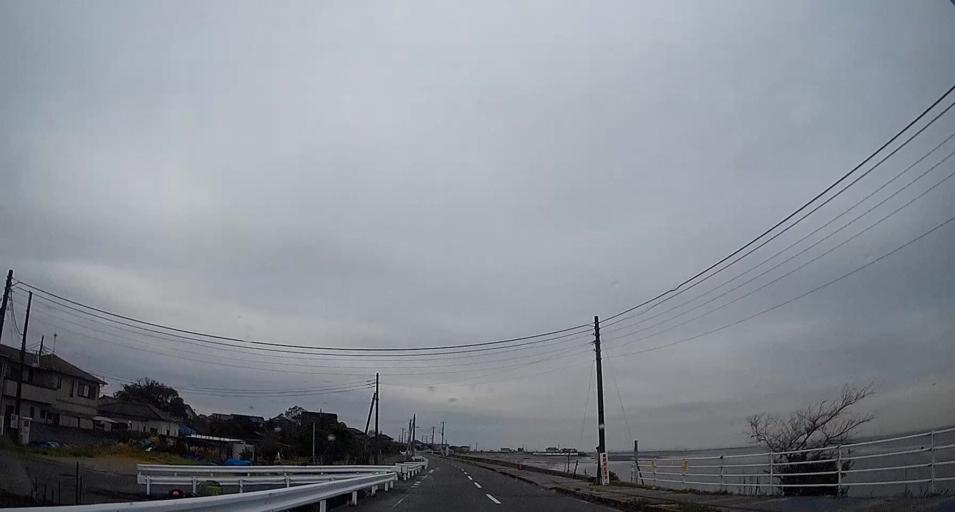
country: JP
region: Chiba
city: Kisarazu
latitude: 35.4348
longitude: 139.9116
